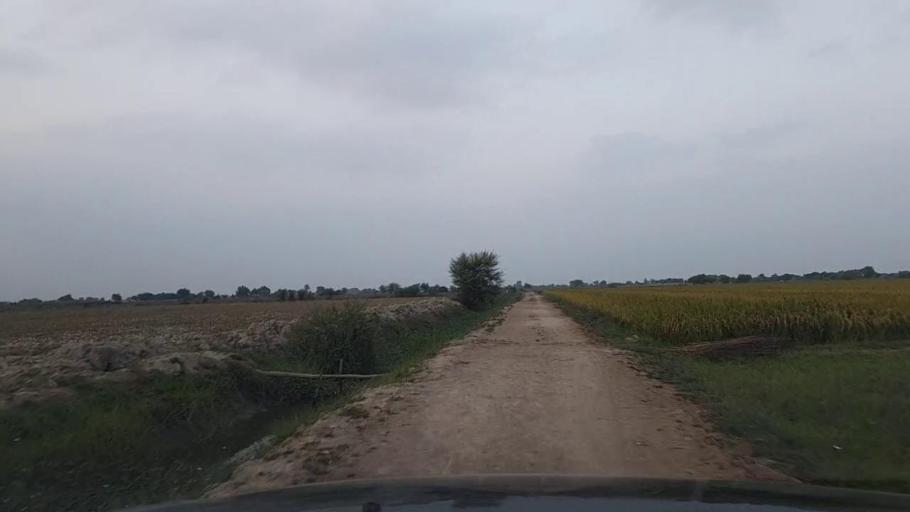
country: PK
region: Sindh
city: Jati
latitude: 24.5063
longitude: 68.3931
